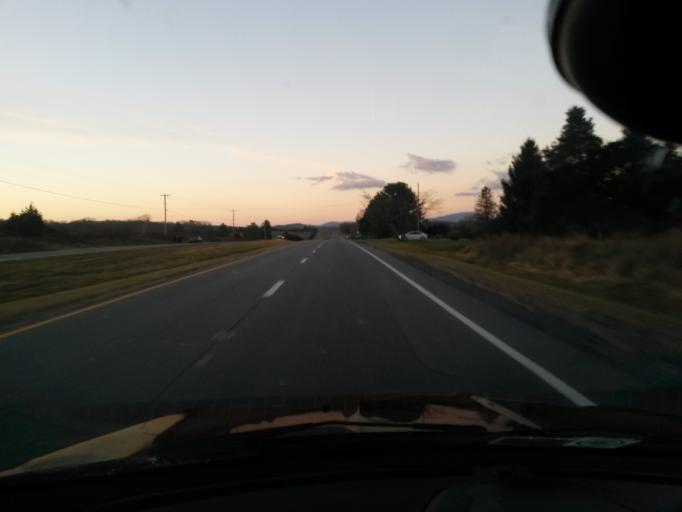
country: US
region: Virginia
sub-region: Botetourt County
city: Fincastle
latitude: 37.5483
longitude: -79.8575
